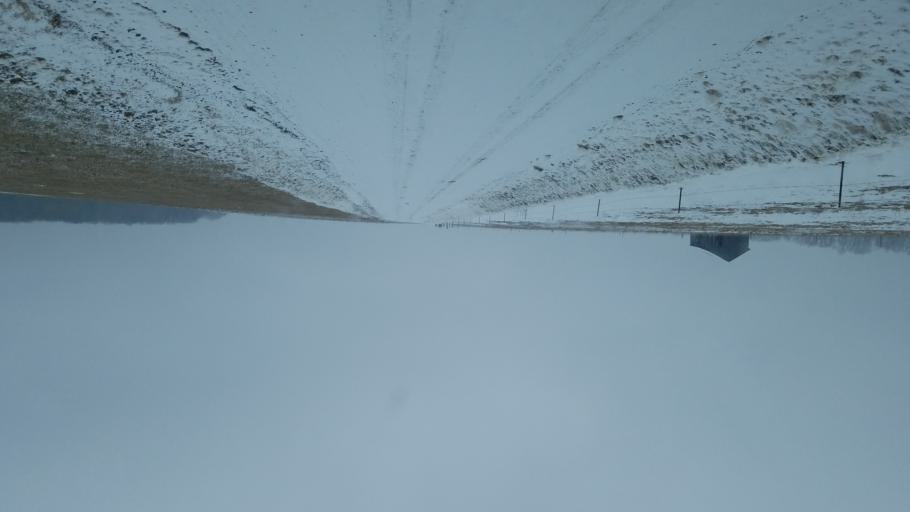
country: US
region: New York
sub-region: Steuben County
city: Canisteo
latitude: 42.1115
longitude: -77.5133
